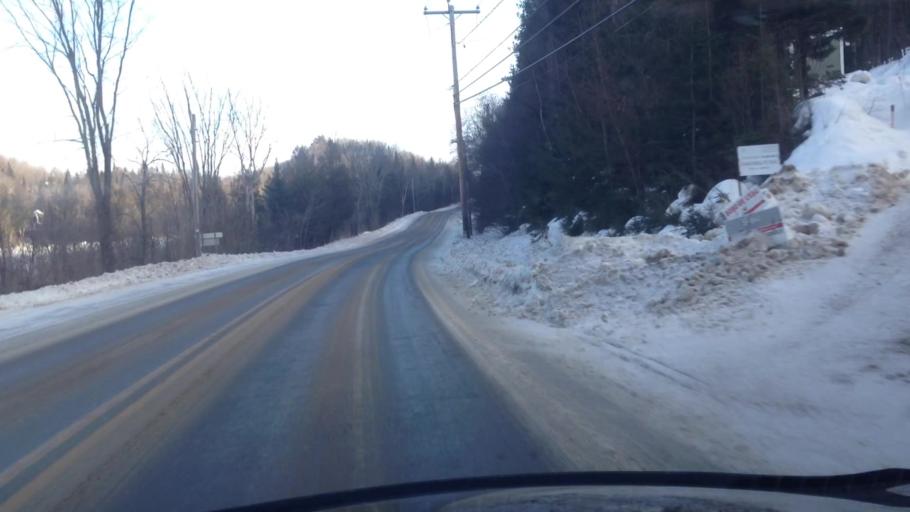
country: CA
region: Quebec
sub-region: Laurentides
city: Sainte-Agathe-des-Monts
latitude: 45.9149
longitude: -74.3648
